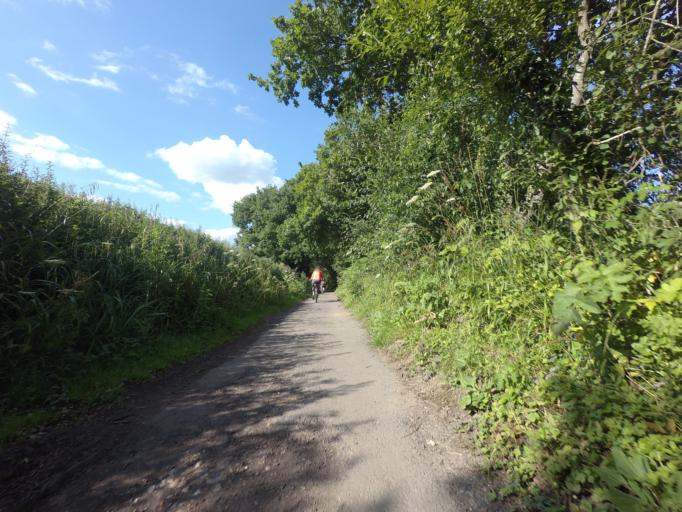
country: GB
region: England
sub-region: East Sussex
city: Hailsham
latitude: 50.8963
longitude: 0.2569
